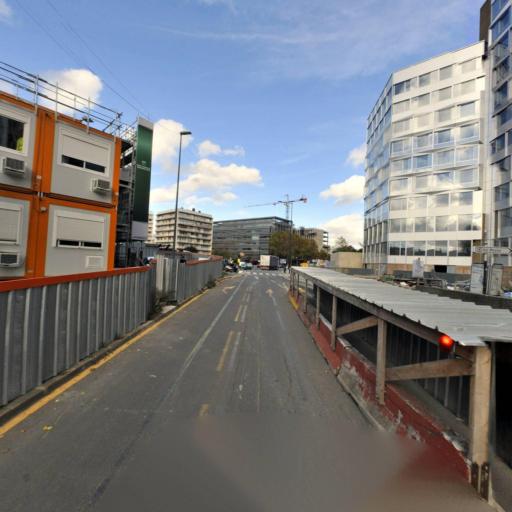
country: FR
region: Ile-de-France
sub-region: Departement des Hauts-de-Seine
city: Sevres
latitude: 48.8289
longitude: 2.2306
